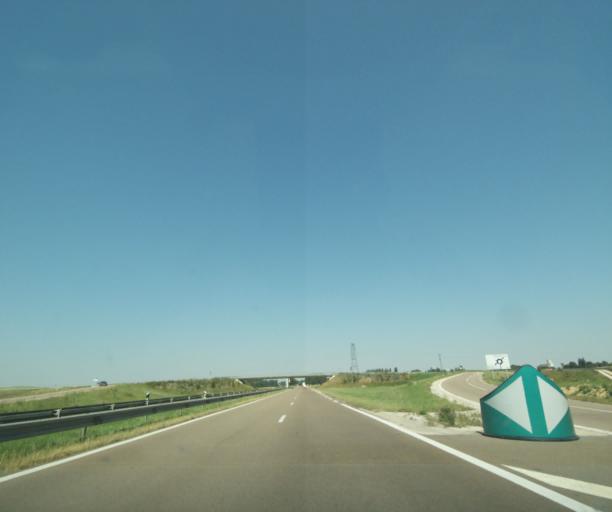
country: FR
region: Champagne-Ardenne
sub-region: Departement de la Marne
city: Pargny-sur-Saulx
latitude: 48.6828
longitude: 4.7429
